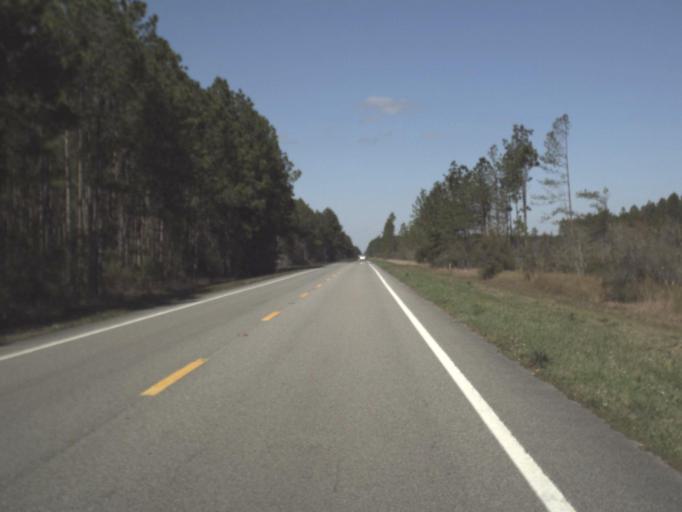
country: US
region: Florida
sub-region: Gulf County
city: Port Saint Joe
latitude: 29.9166
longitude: -85.2014
